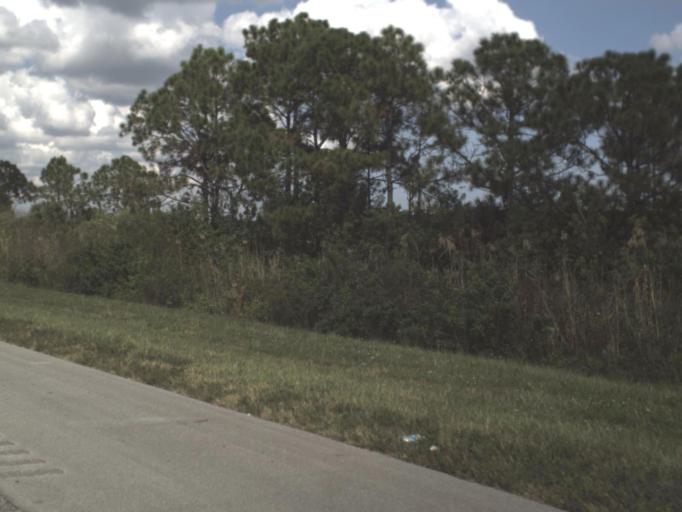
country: US
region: Florida
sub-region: Palm Beach County
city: Tequesta
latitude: 27.0010
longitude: -80.2034
